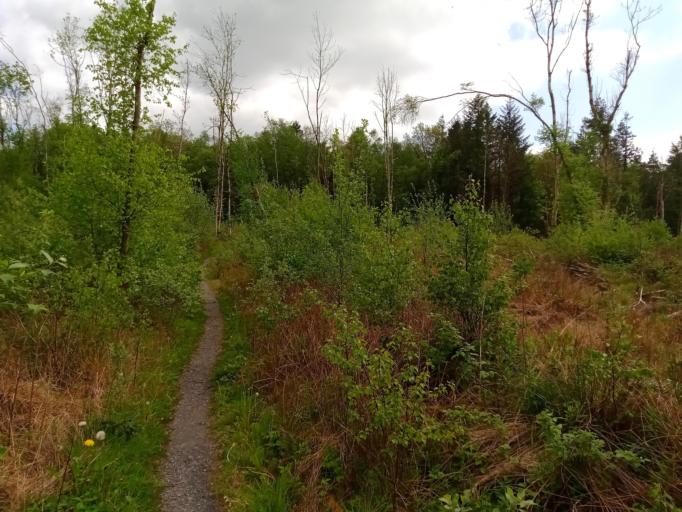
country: IE
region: Leinster
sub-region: Kilkenny
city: Castlecomer
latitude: 52.8162
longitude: -7.2026
